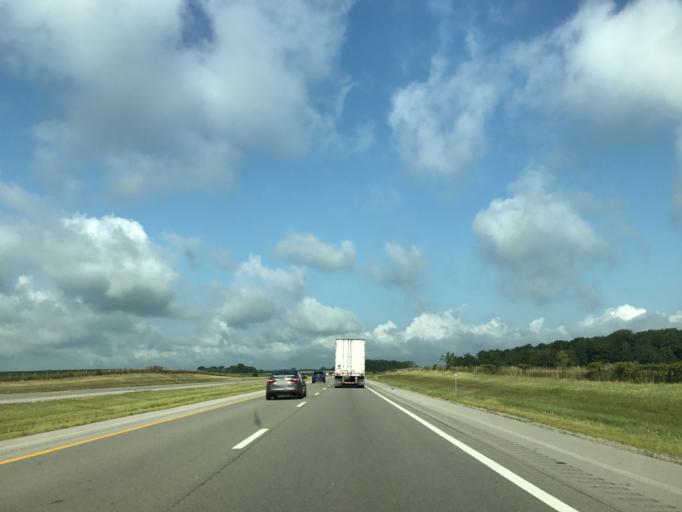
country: US
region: Ohio
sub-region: Williams County
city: Montpelier
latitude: 41.6242
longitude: -84.6987
